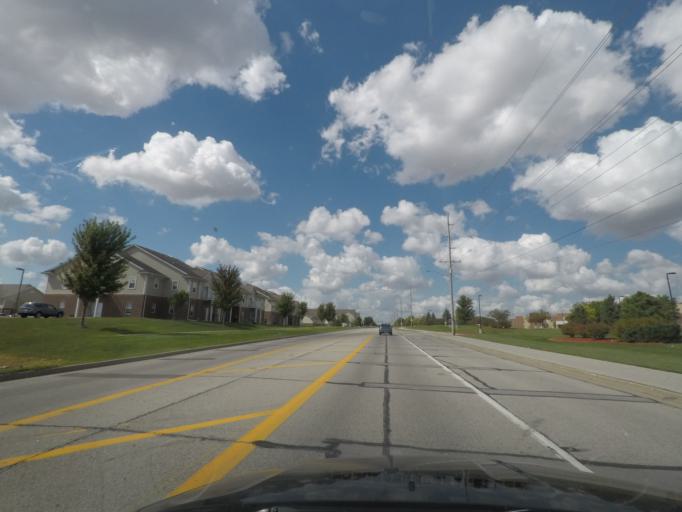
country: US
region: Iowa
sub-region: Story County
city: Ames
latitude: 42.0120
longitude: -93.6687
